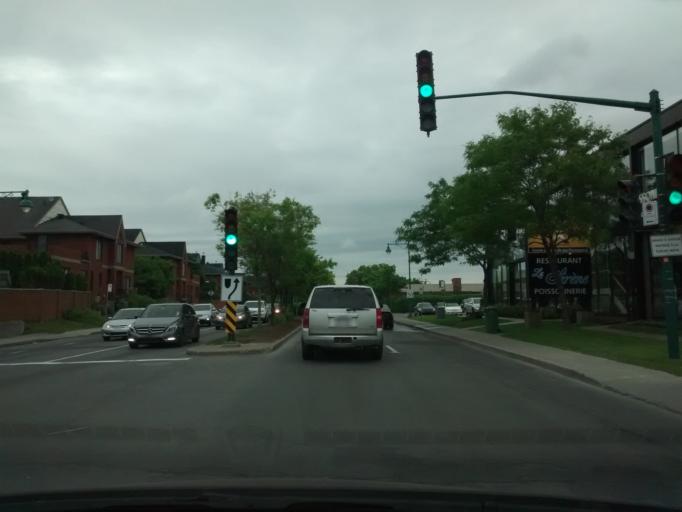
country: CA
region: Quebec
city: Mont-Royal
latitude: 45.5159
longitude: -73.6308
